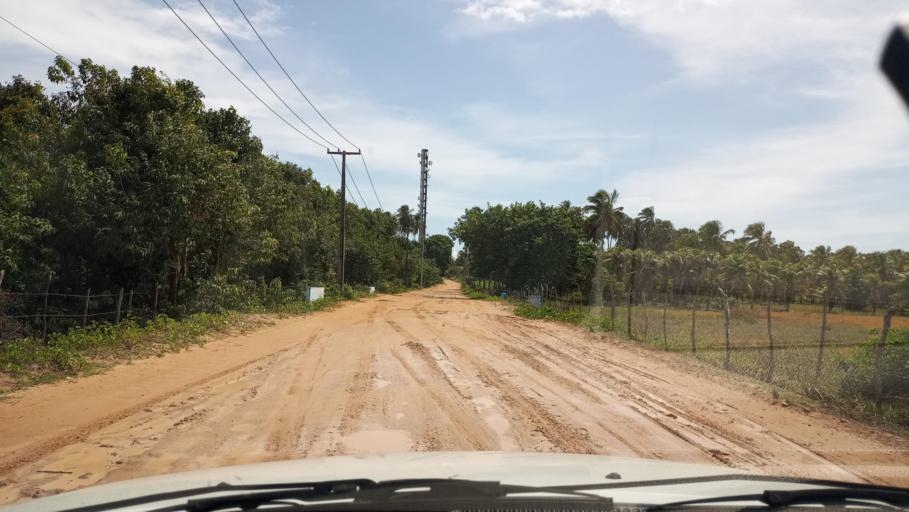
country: BR
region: Rio Grande do Norte
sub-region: Maxaranguape
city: Sao Miguel
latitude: -5.4638
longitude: -35.2948
